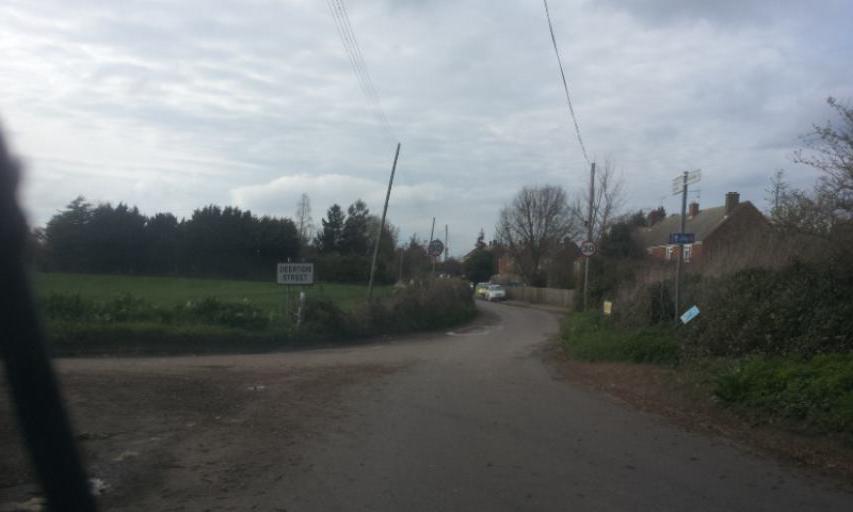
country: GB
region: England
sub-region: Kent
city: Teynham
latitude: 51.3264
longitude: 0.8296
